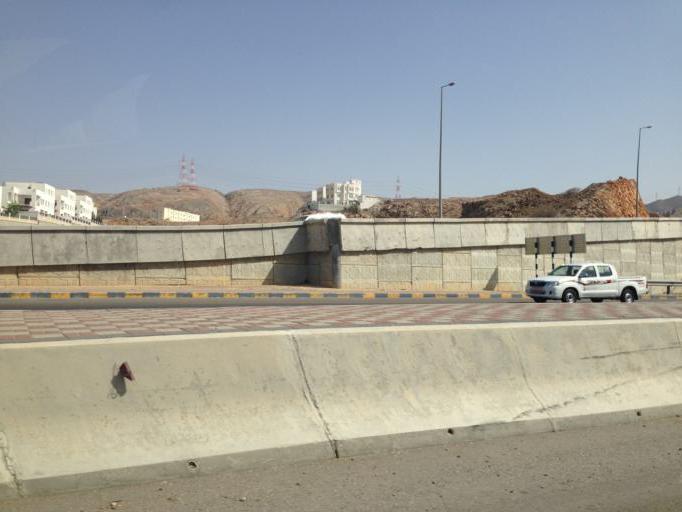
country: OM
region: Muhafazat Masqat
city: Muscat
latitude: 23.6050
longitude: 58.4900
